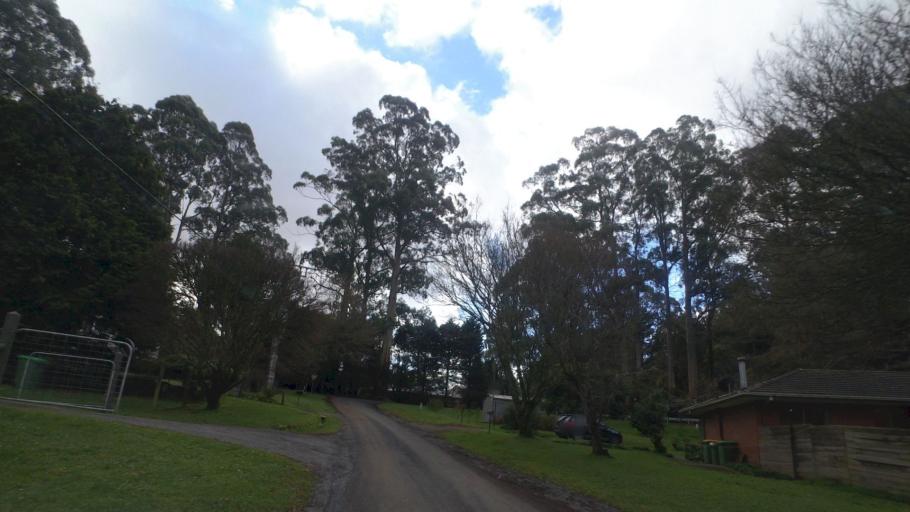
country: AU
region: Victoria
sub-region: Yarra Ranges
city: Olinda
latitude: -37.8452
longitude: 145.3553
